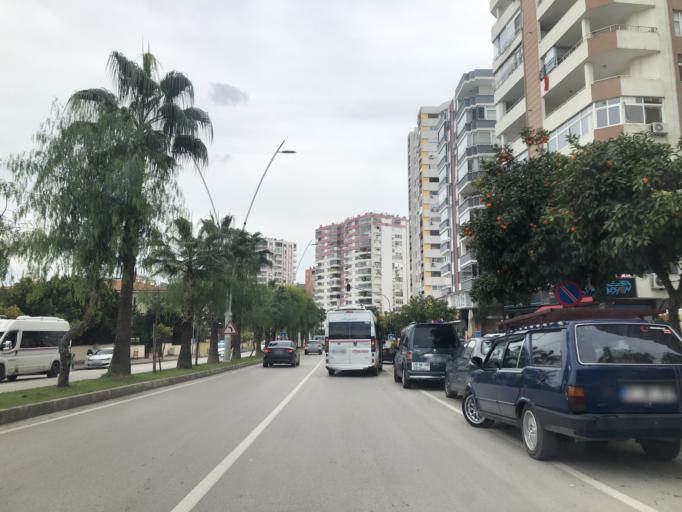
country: TR
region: Adana
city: Adana
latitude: 37.0531
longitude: 35.2909
